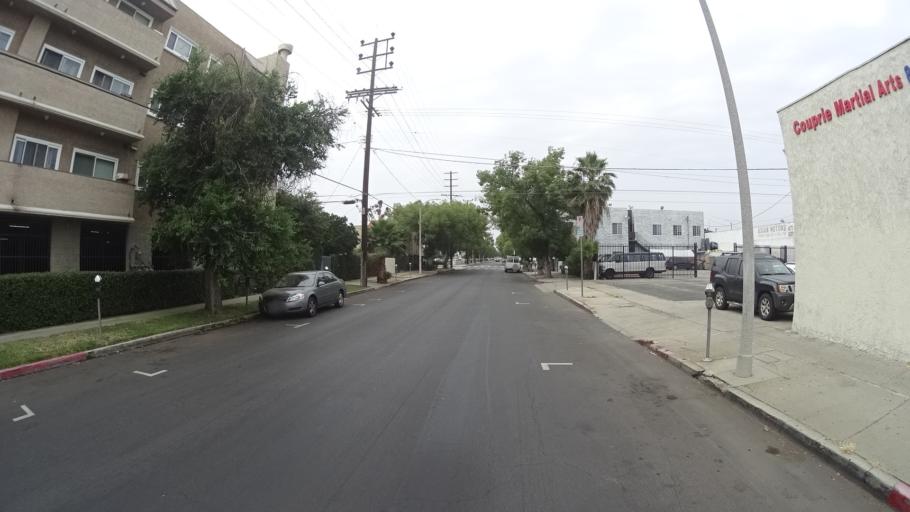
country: US
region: California
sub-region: Los Angeles County
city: Van Nuys
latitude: 34.1840
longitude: -118.4509
